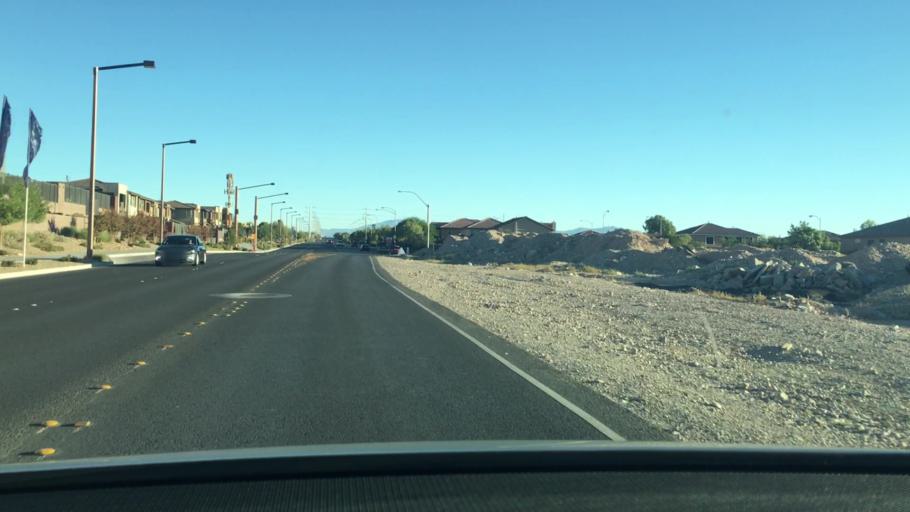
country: US
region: Nevada
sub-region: Clark County
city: Summerlin South
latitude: 36.0763
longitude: -115.3157
